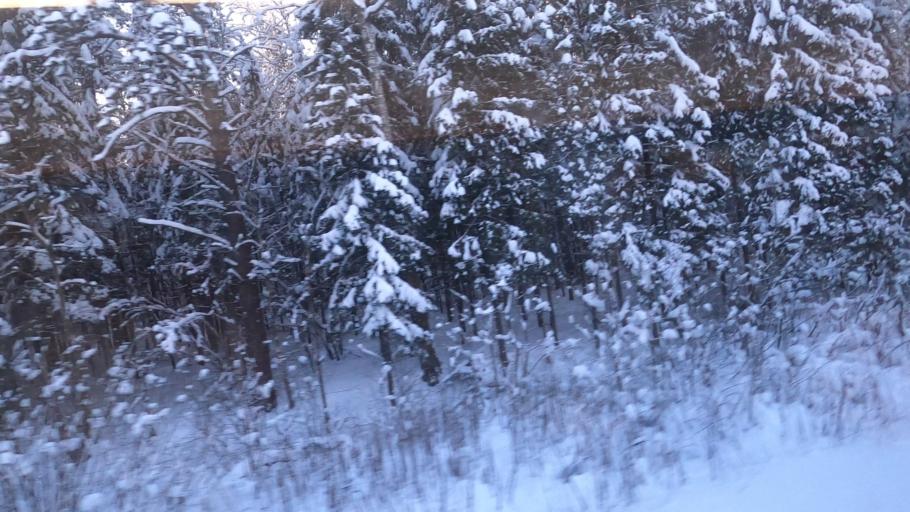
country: RU
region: Moskovskaya
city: Novo-Nikol'skoye
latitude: 56.6296
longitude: 37.5636
